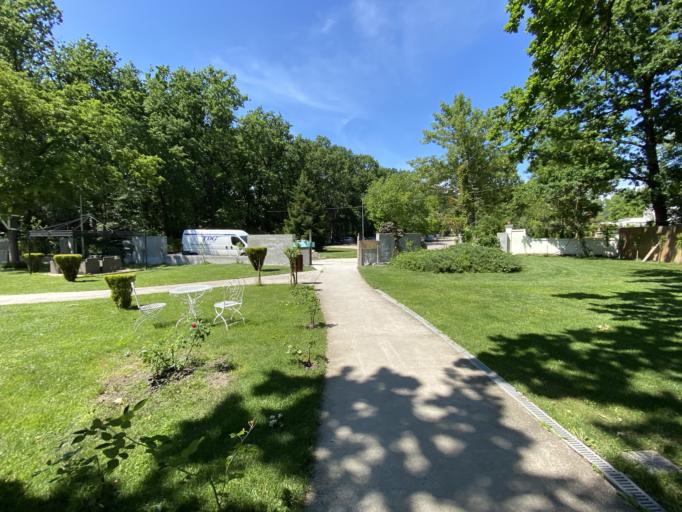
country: RO
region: Ilfov
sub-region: Comuna Cernica
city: Caldararu
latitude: 44.4362
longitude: 26.2457
